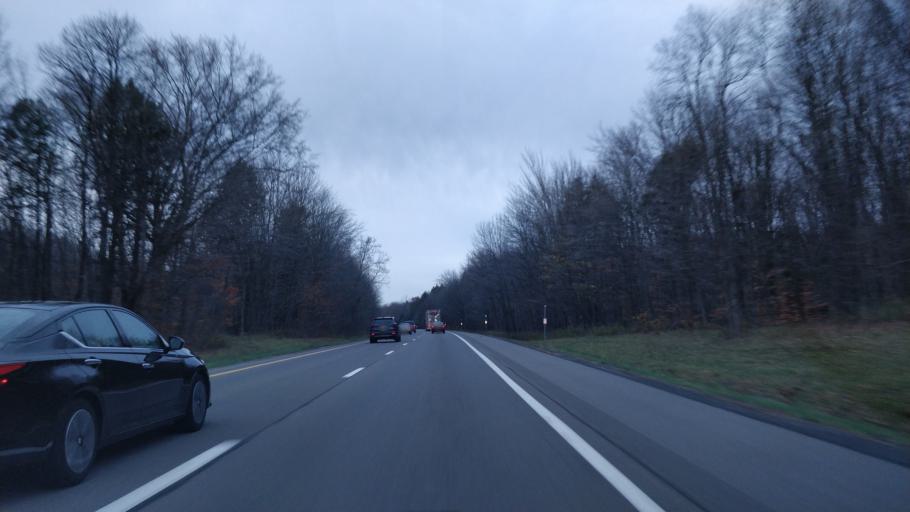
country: US
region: New York
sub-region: Oswego County
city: Central Square
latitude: 43.3852
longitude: -76.1192
